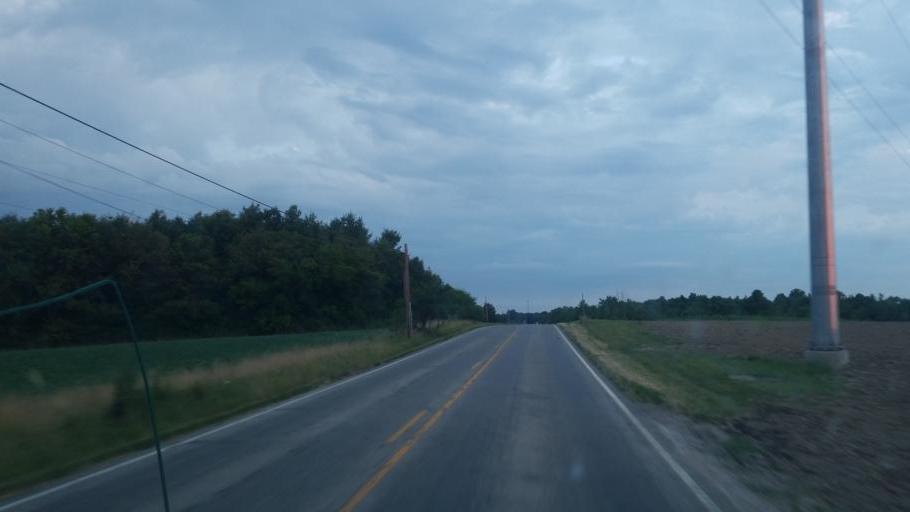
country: US
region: Ohio
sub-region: Defiance County
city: Hicksville
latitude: 41.3383
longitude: -84.8244
